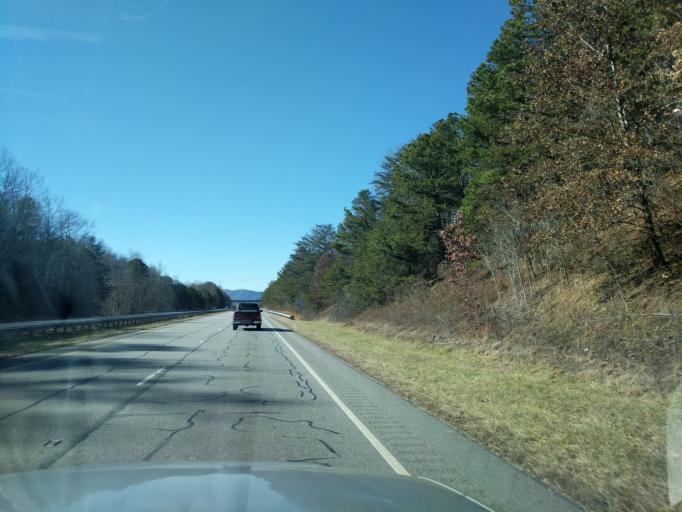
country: US
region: North Carolina
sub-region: Swain County
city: Cherokee
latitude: 35.4373
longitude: -83.3747
